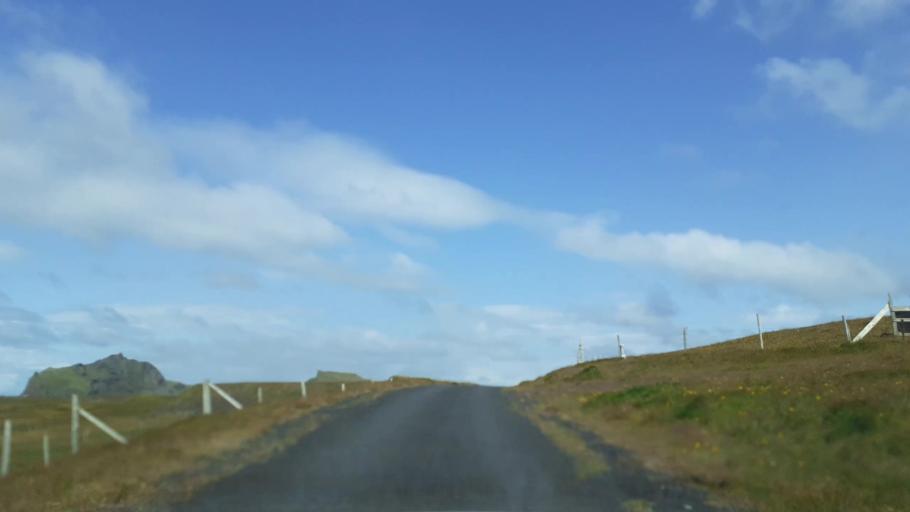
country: IS
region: South
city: Vestmannaeyjar
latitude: 63.4178
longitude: -20.2813
